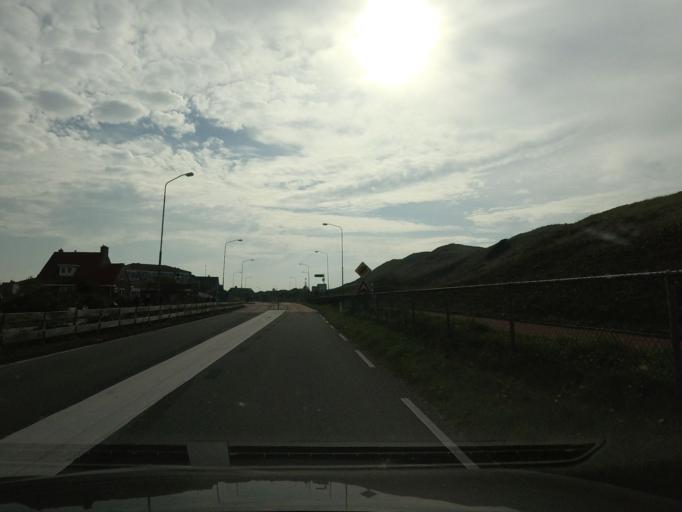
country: NL
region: North Holland
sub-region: Gemeente Schagen
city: Schagen
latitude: 52.8406
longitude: 4.6947
